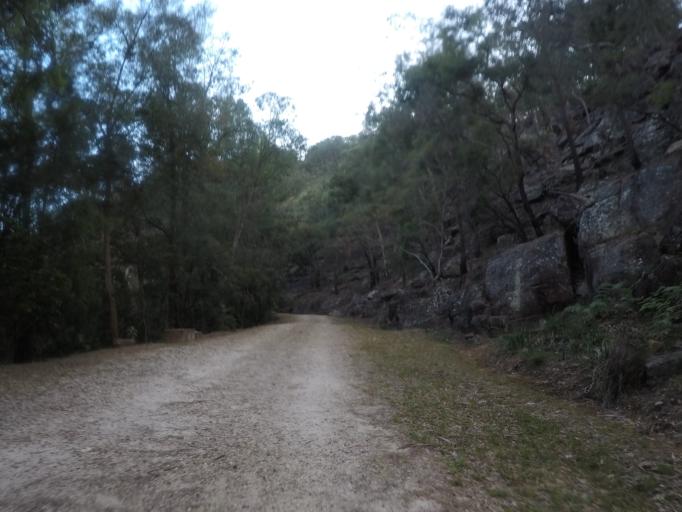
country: AU
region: New South Wales
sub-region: Hornsby Shire
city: Glenorie
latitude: -33.3737
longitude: 150.9846
